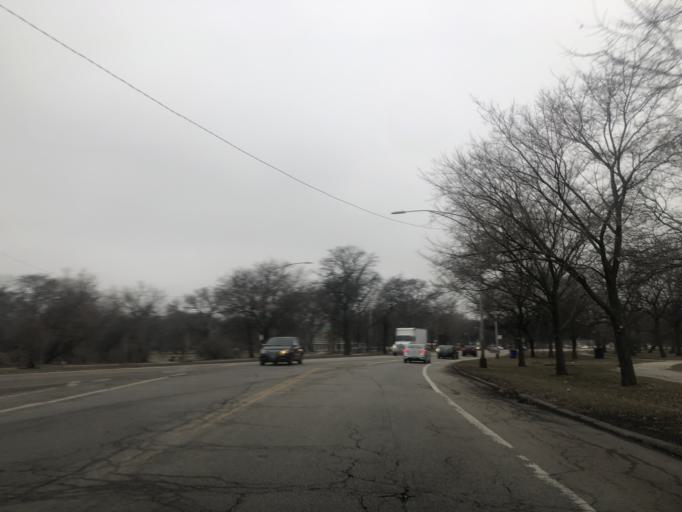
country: US
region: Illinois
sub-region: Cook County
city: Chicago
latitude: 41.7933
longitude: -87.6104
